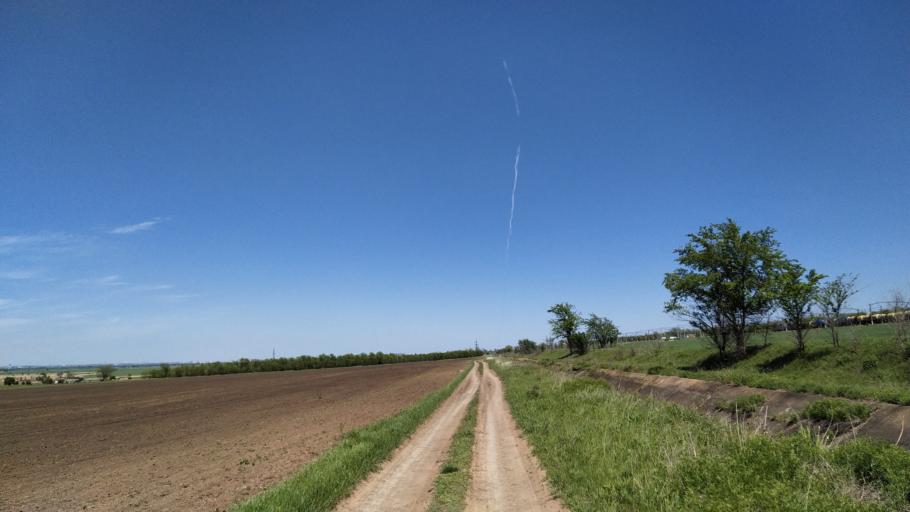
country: RU
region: Rostov
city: Kuleshovka
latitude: 47.0297
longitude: 39.6332
